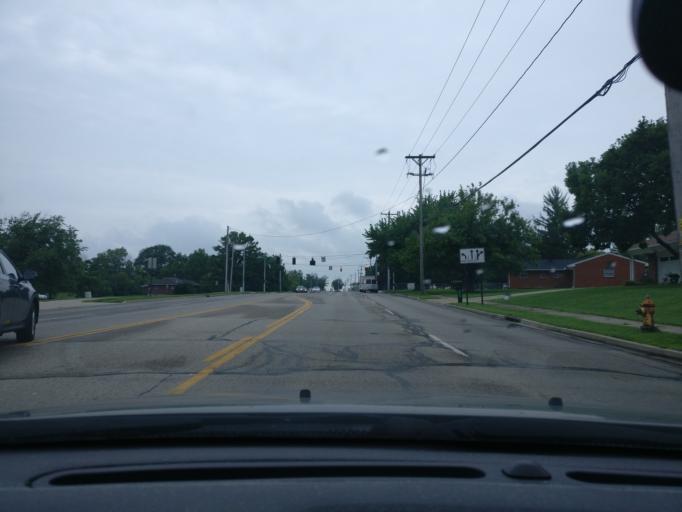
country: US
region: Ohio
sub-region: Montgomery County
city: West Carrollton City
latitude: 39.6308
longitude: -84.2350
